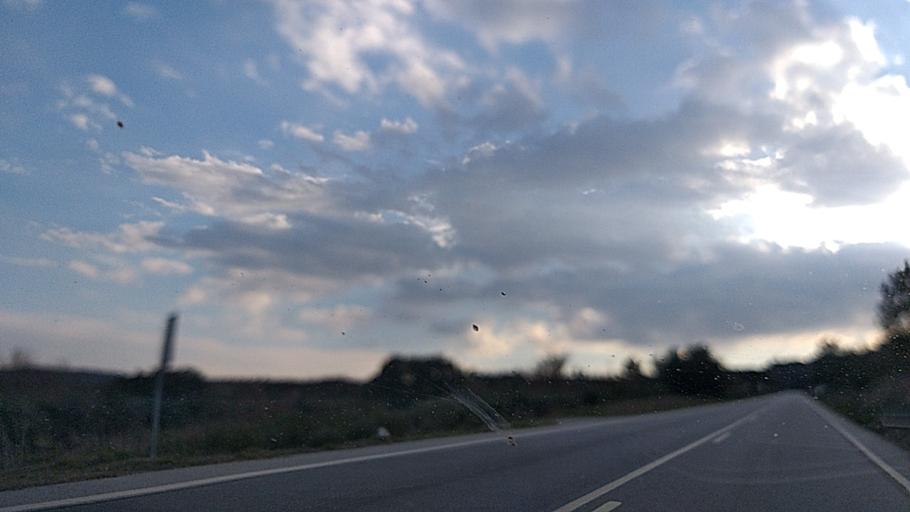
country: ES
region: Castille and Leon
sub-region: Provincia de Salamanca
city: Aldea del Obispo
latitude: 40.6938
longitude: -6.9359
